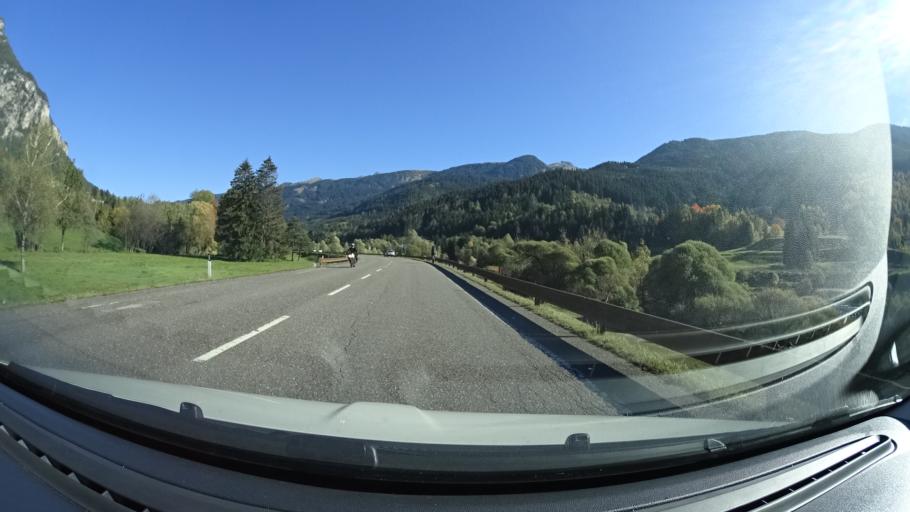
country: IT
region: Trentino-Alto Adige
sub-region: Provincia di Trento
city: Tesero
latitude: 46.2828
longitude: 11.5238
